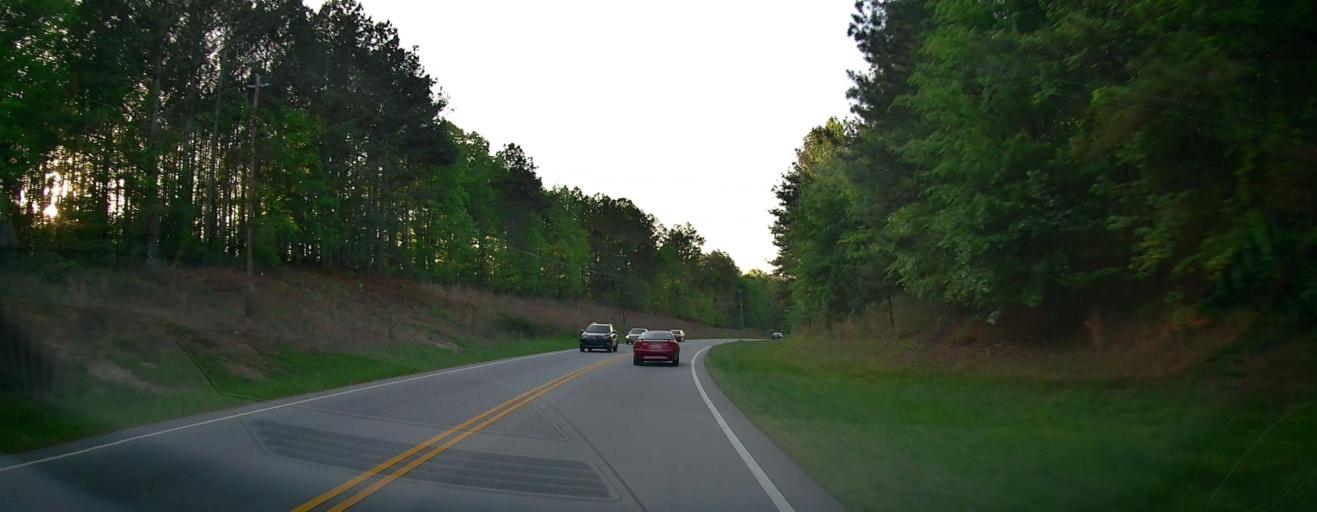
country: US
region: Georgia
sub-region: Newton County
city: Porterdale
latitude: 33.5591
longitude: -83.8997
